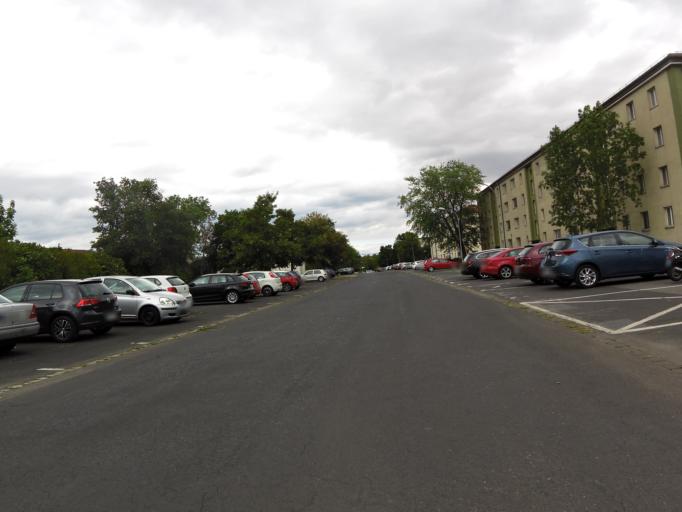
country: DE
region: Bavaria
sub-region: Regierungsbezirk Unterfranken
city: Gerbrunn
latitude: 49.7854
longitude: 9.9768
